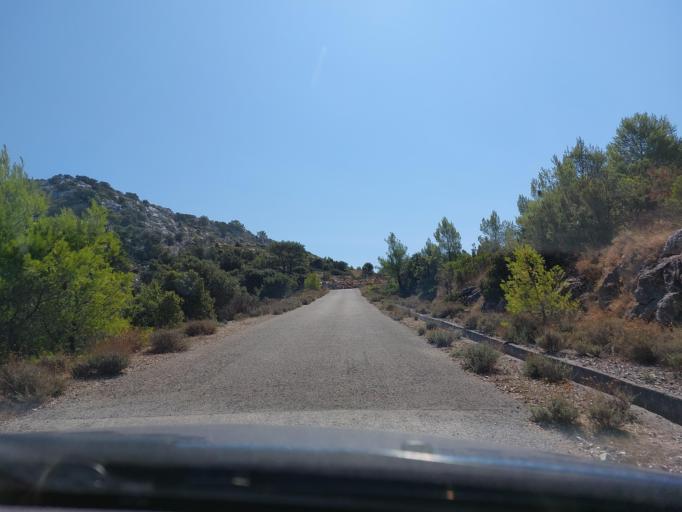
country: HR
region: Dubrovacko-Neretvanska
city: Smokvica
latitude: 42.7461
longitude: 16.8537
